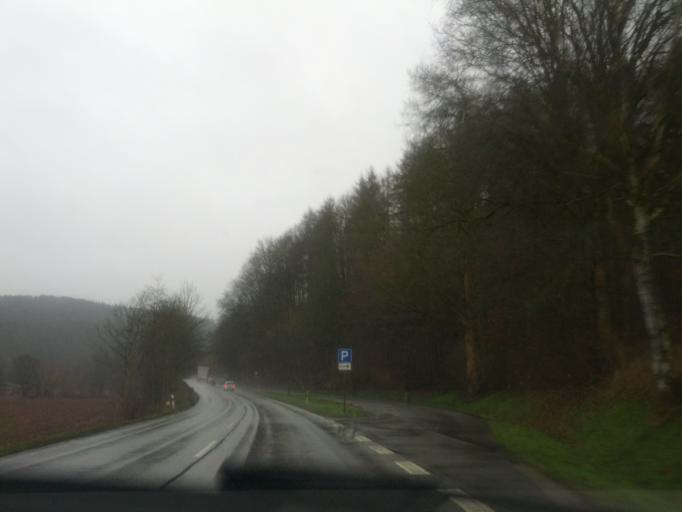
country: DE
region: Hesse
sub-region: Regierungsbezirk Kassel
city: Sontra
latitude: 51.0975
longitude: 9.9705
